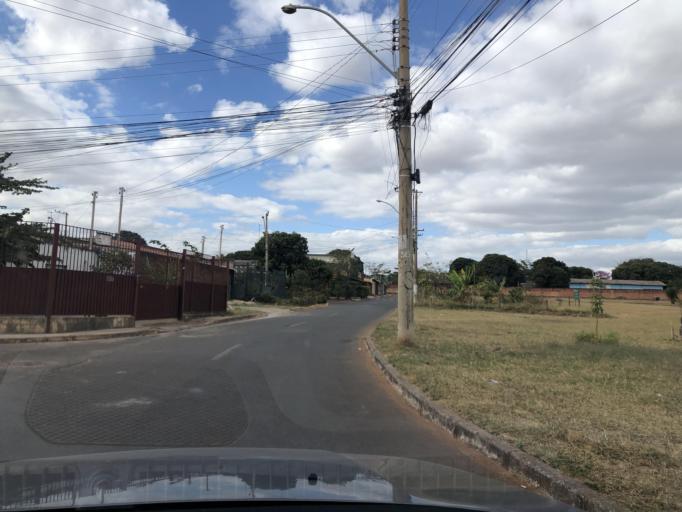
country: BR
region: Federal District
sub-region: Brasilia
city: Brasilia
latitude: -15.8926
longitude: -48.1190
